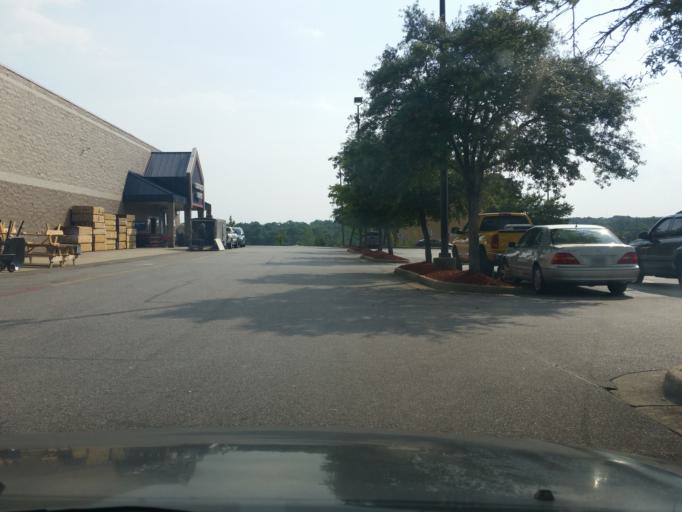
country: US
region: Florida
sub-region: Escambia County
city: Brent
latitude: 30.4802
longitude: -87.2141
